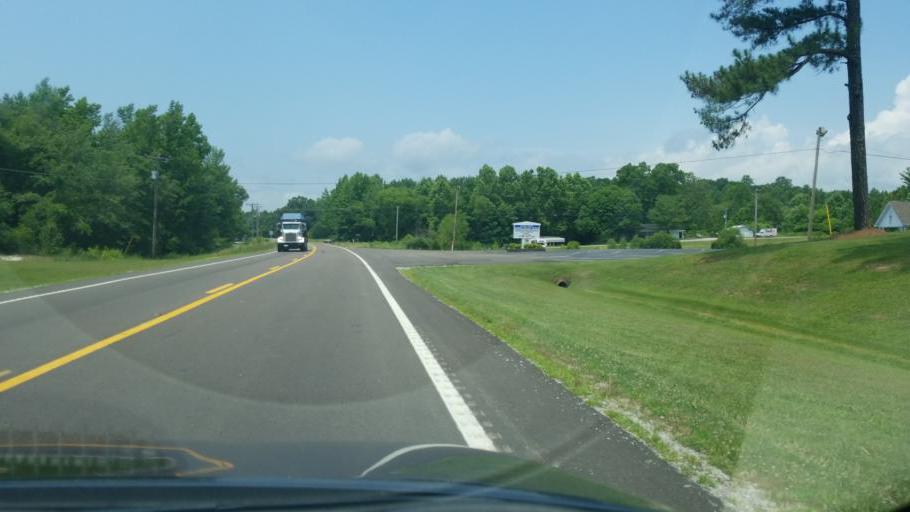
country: US
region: Tennessee
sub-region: Benton County
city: Camden
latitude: 36.0460
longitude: -88.1659
